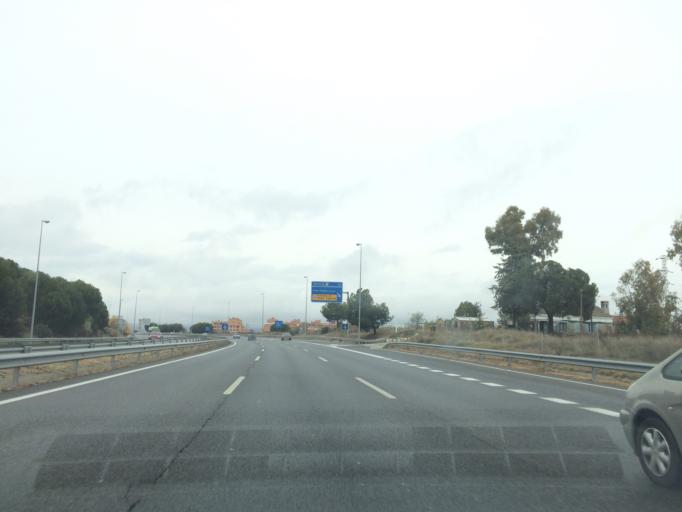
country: ES
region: Madrid
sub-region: Provincia de Madrid
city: Tres Cantos
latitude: 40.5919
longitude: -3.7124
